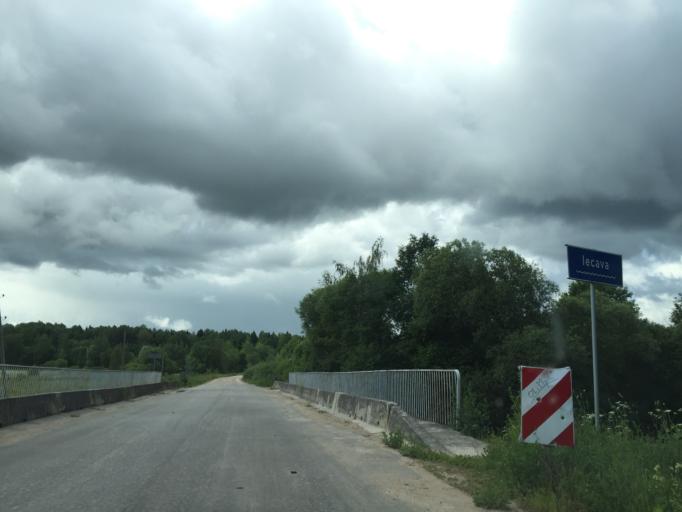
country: LV
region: Lecava
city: Iecava
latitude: 56.6233
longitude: 24.1839
